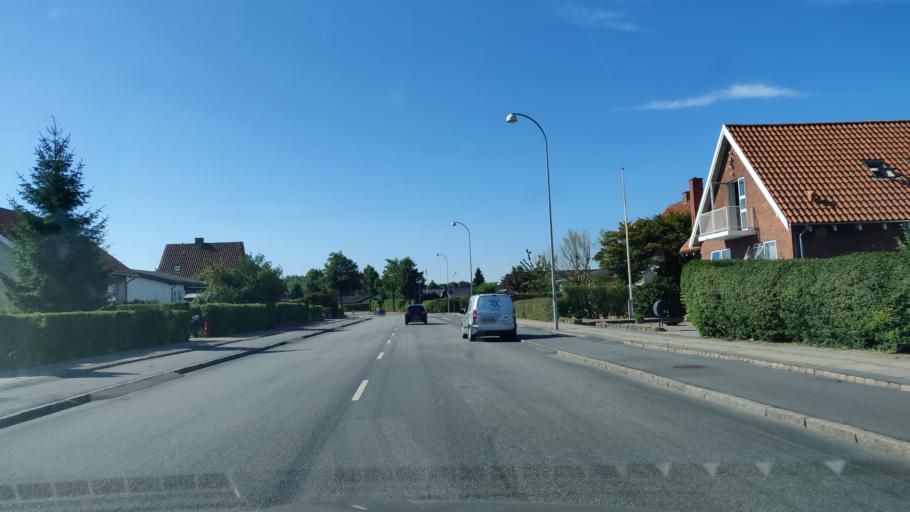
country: DK
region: Zealand
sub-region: Roskilde Kommune
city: Roskilde
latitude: 55.6349
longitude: 12.1017
